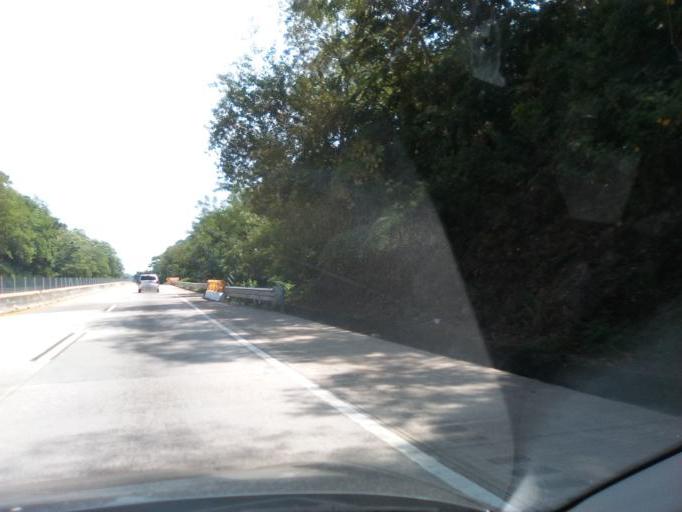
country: MX
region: Guerrero
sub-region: Acapulco de Juarez
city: Pueblo Madero (El Playon)
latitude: 17.1029
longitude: -99.5891
